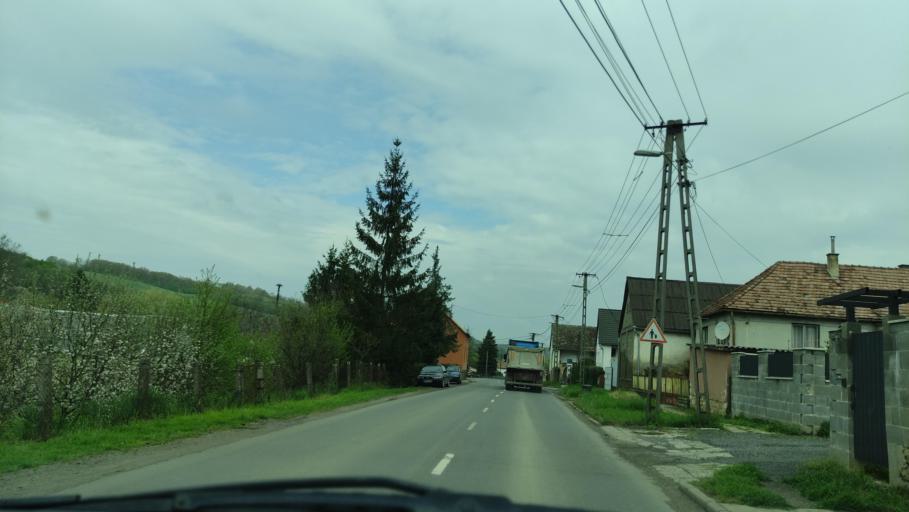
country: HU
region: Baranya
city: Komlo
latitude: 46.2117
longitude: 18.2445
